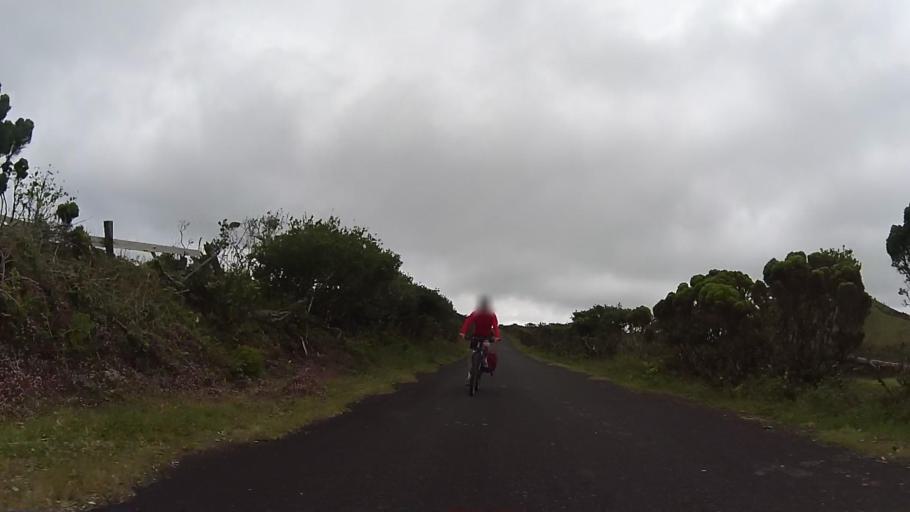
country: PT
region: Azores
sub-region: Sao Roque do Pico
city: Sao Roque do Pico
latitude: 38.4662
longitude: -28.2931
